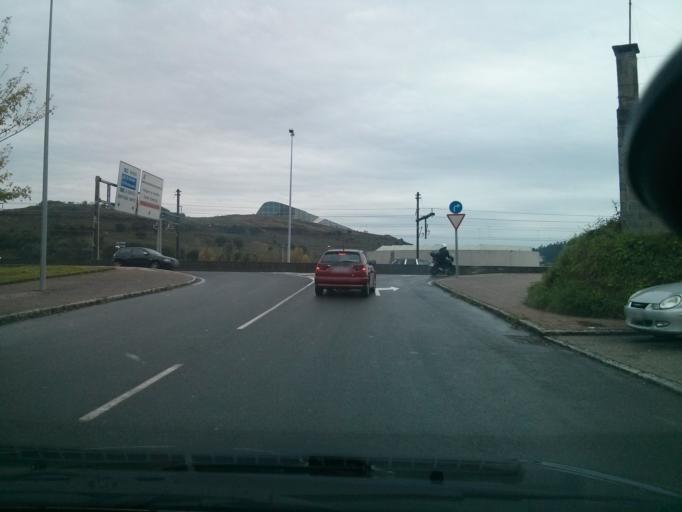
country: ES
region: Galicia
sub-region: Provincia da Coruna
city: Santiago de Compostela
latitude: 42.8794
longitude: -8.5305
